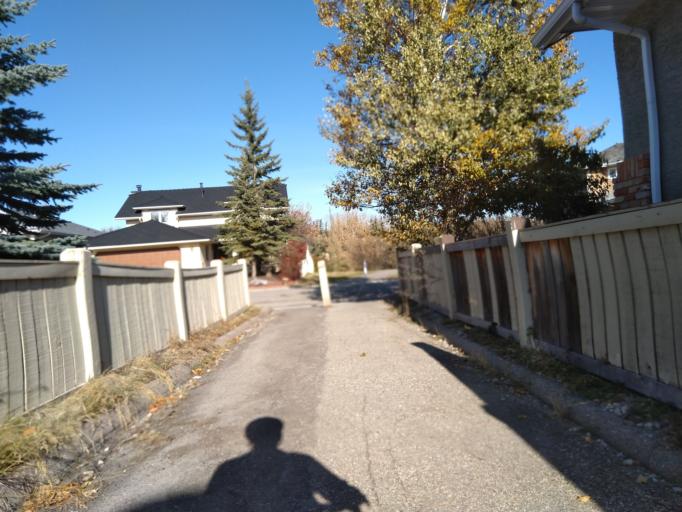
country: CA
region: Alberta
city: Calgary
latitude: 51.1378
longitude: -114.1534
